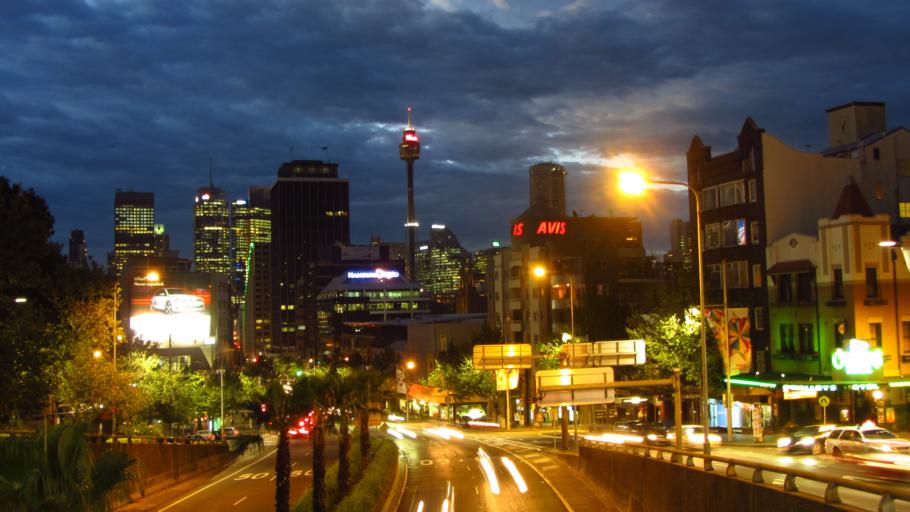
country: AU
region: New South Wales
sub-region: City of Sydney
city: Darlinghurst
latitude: -33.8755
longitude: 151.2218
